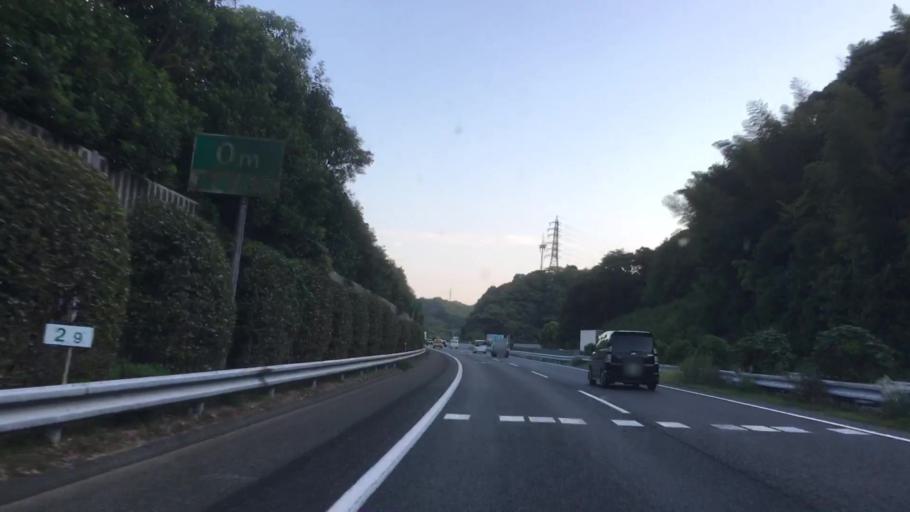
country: JP
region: Yamaguchi
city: Shimonoseki
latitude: 33.9009
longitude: 130.9714
